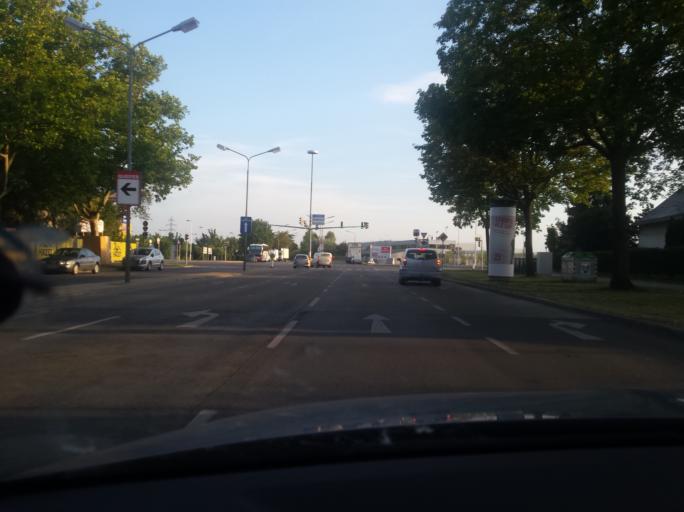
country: AT
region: Lower Austria
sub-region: Politischer Bezirk Wien-Umgebung
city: Schwechat
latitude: 48.1492
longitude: 16.4619
